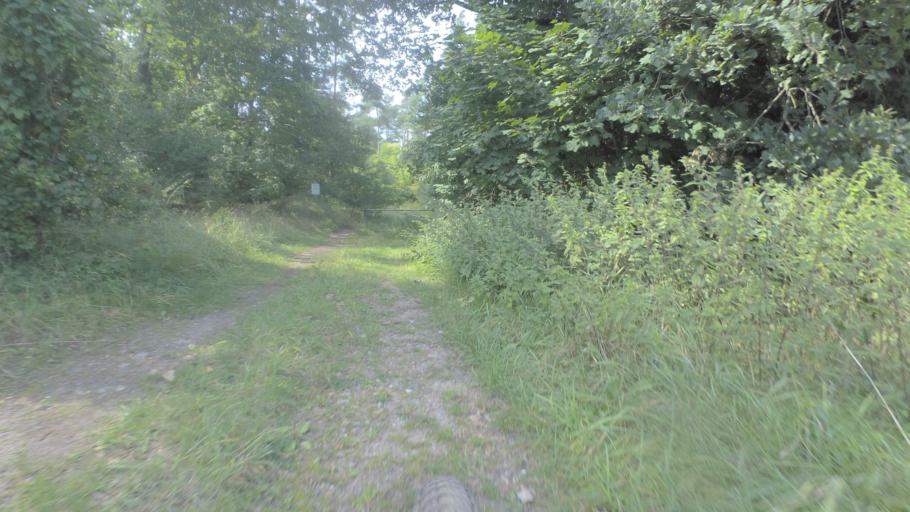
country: DE
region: Brandenburg
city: Rangsdorf
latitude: 52.2467
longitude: 13.4066
